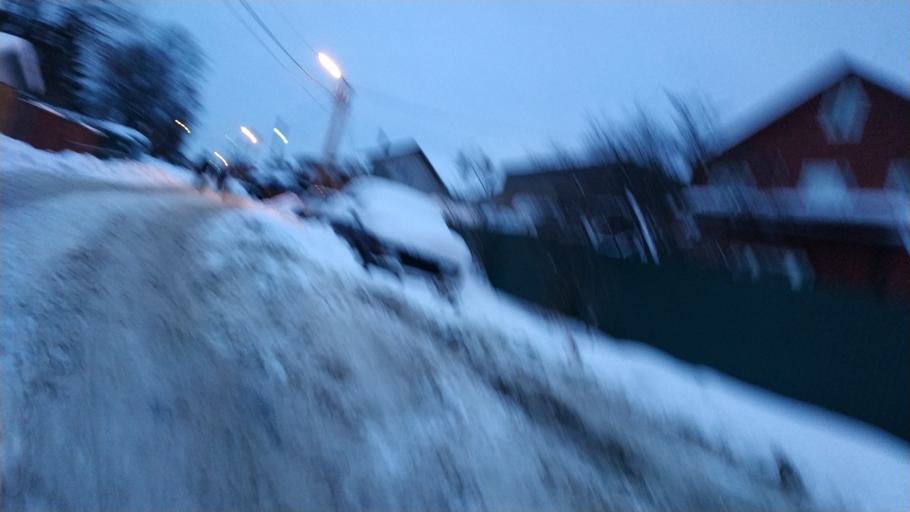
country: RU
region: Moskovskaya
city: Nemchinovka
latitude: 55.7343
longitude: 37.3537
